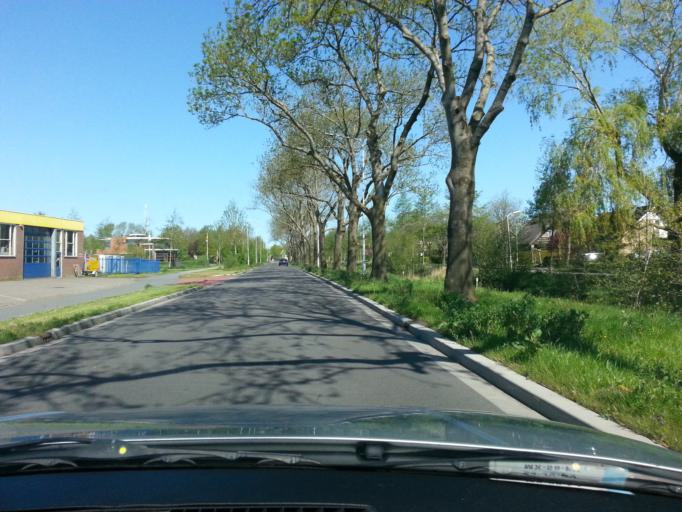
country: NL
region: Friesland
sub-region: Gemeente Achtkarspelen
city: Buitenpost
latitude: 53.2458
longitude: 6.1531
